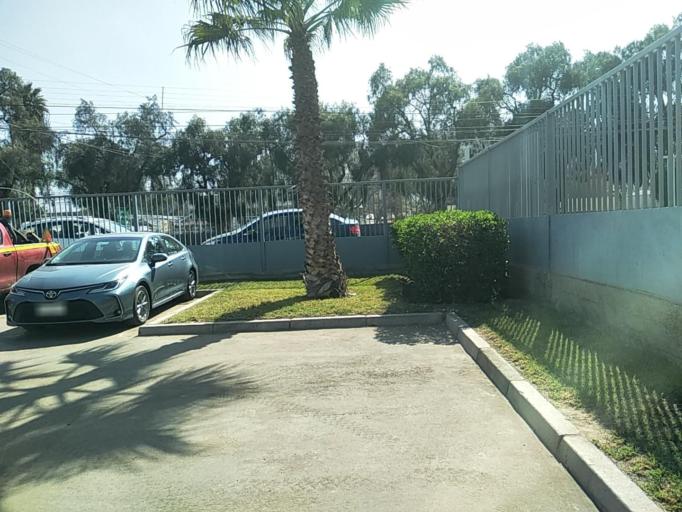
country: CL
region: Atacama
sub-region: Provincia de Copiapo
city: Copiapo
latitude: -27.3628
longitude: -70.3464
